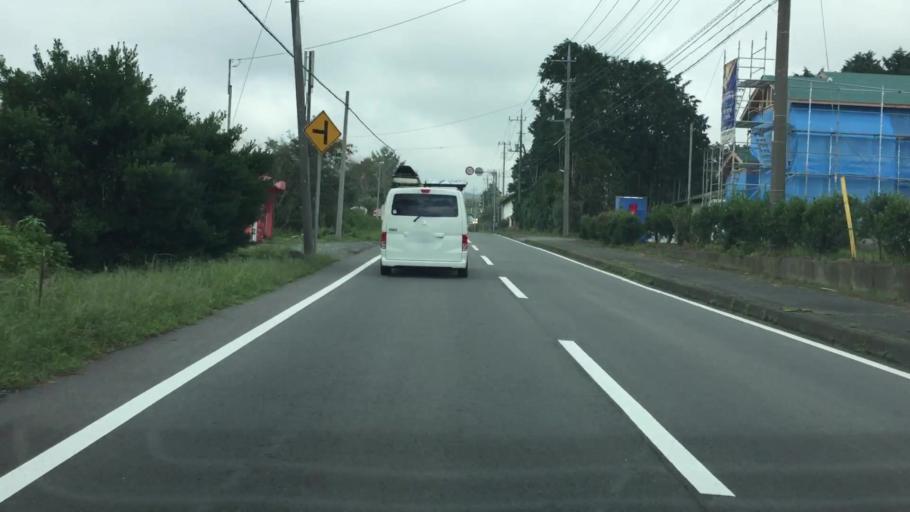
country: JP
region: Shizuoka
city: Fujinomiya
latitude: 35.3394
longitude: 138.5948
